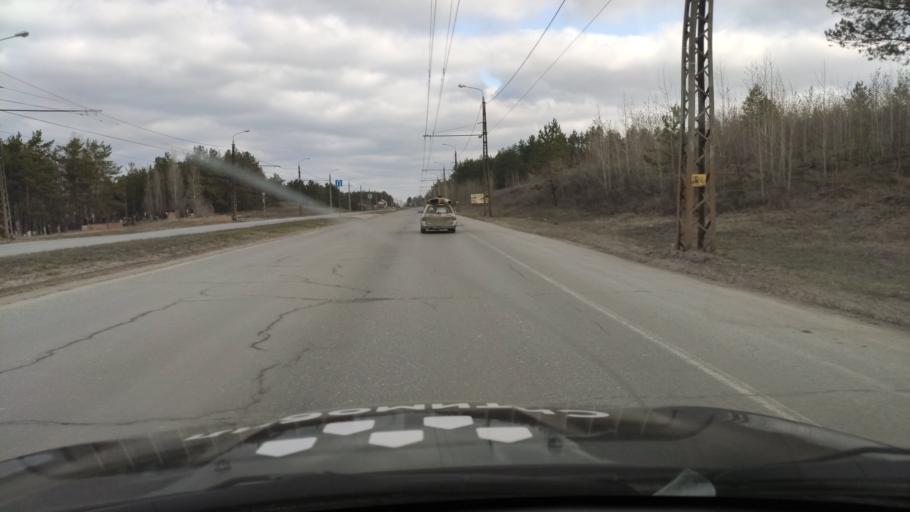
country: RU
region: Samara
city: Zhigulevsk
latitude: 53.5238
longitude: 49.5442
